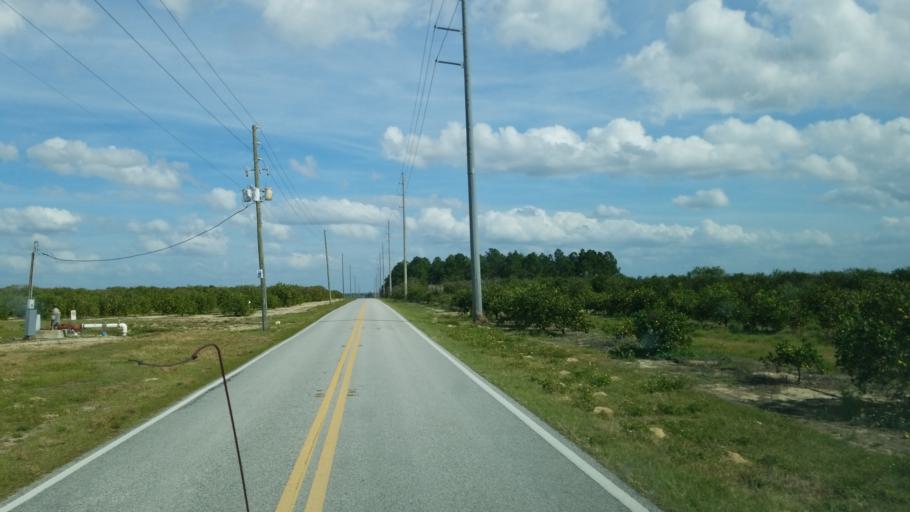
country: US
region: Florida
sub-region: Polk County
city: Dundee
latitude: 27.9828
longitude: -81.5854
